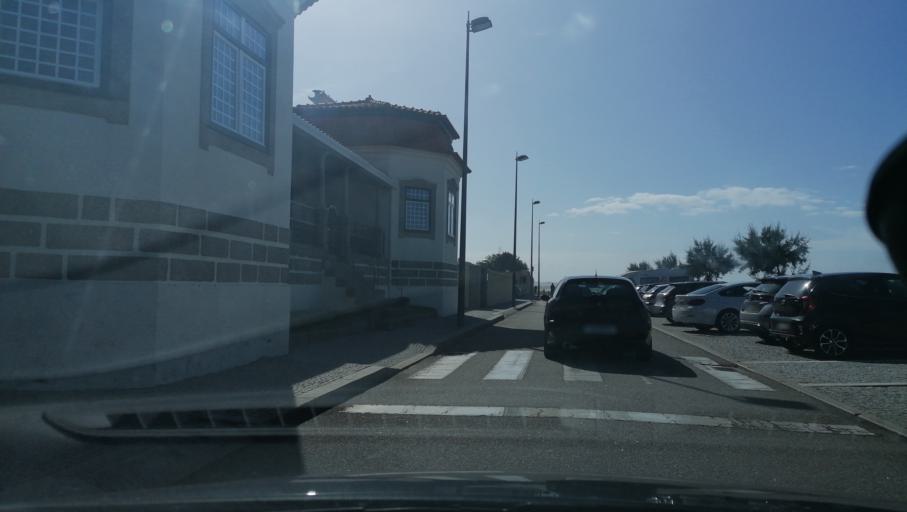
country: PT
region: Porto
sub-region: Vila Nova de Gaia
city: Arcozelo
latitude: 41.0389
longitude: -8.6494
